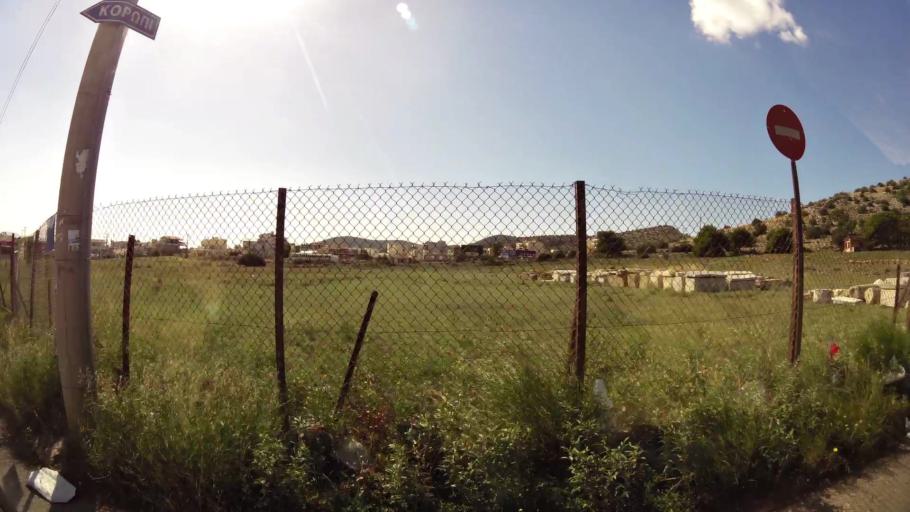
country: GR
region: Attica
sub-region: Nomarchia Anatolikis Attikis
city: Vari
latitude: 37.8365
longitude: 23.8046
